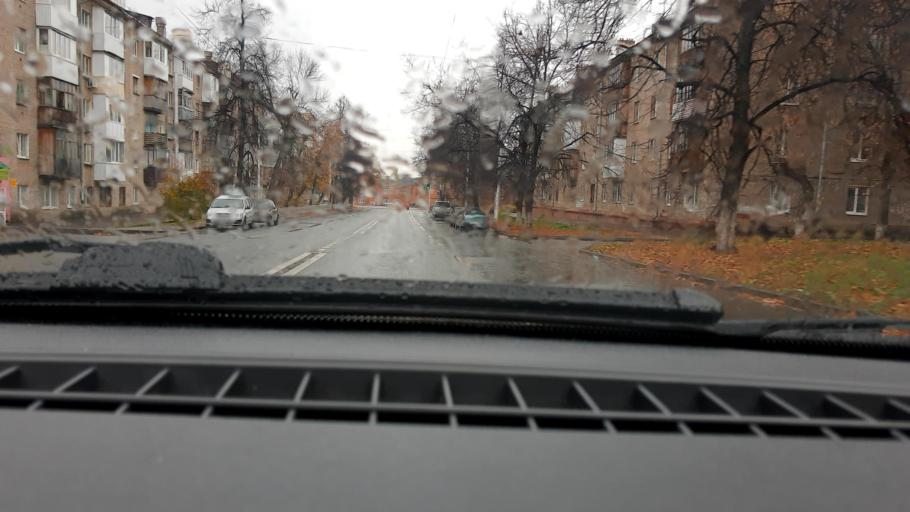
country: RU
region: Bashkortostan
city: Ufa
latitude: 54.8165
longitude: 56.1054
